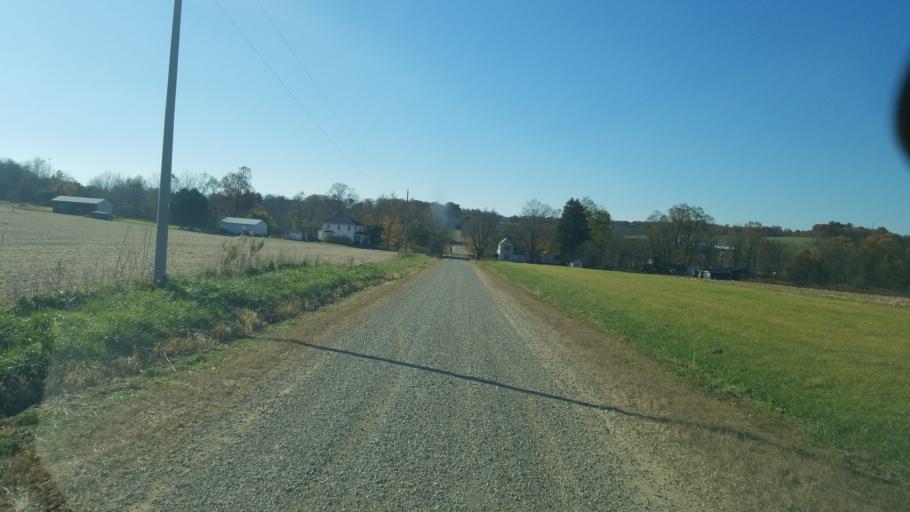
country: US
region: Ohio
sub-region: Knox County
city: Danville
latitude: 40.4307
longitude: -82.2976
